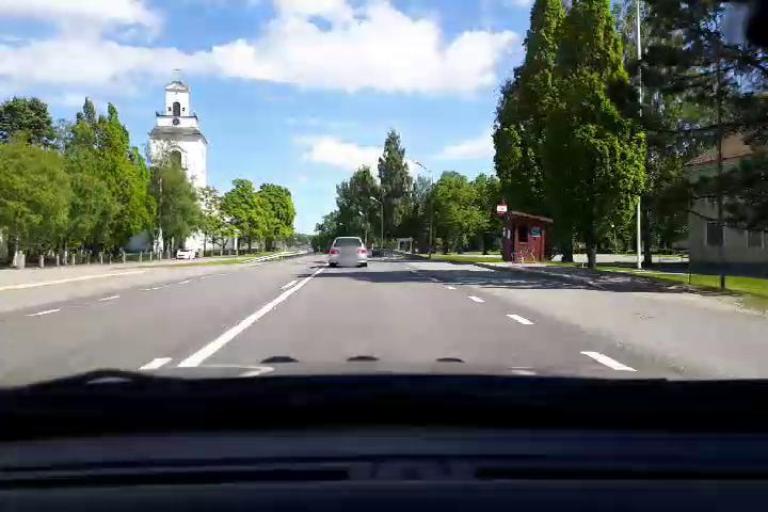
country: SE
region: Gaevleborg
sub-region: Hudiksvalls Kommun
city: Sorforsa
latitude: 61.7344
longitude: 16.9363
